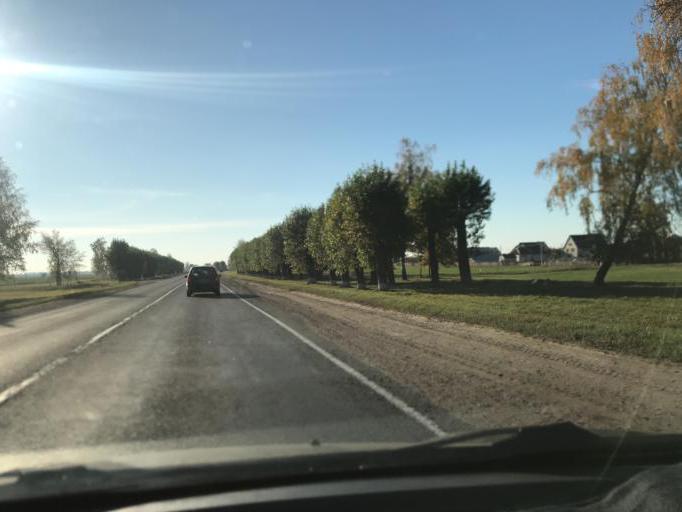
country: BY
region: Minsk
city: Slutsk
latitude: 53.0576
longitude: 27.6664
